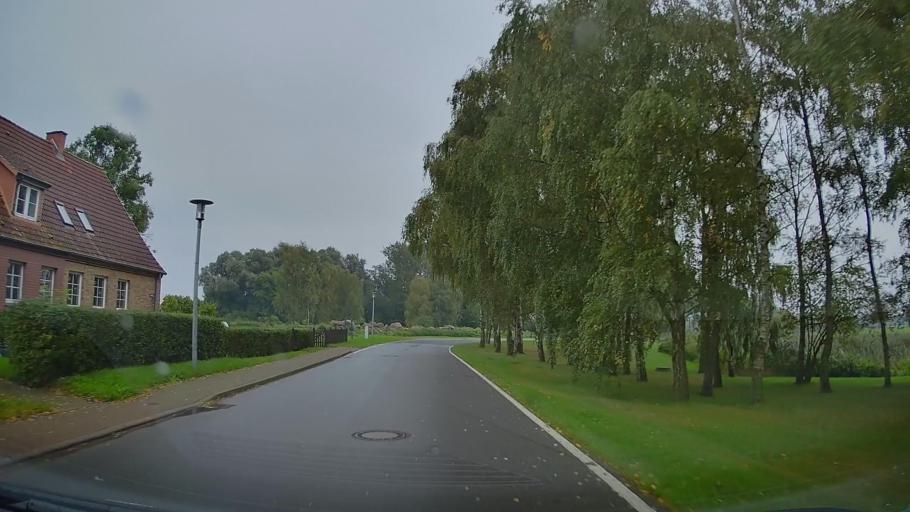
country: DE
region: Mecklenburg-Vorpommern
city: Kalkhorst
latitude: 54.0005
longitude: 11.0499
